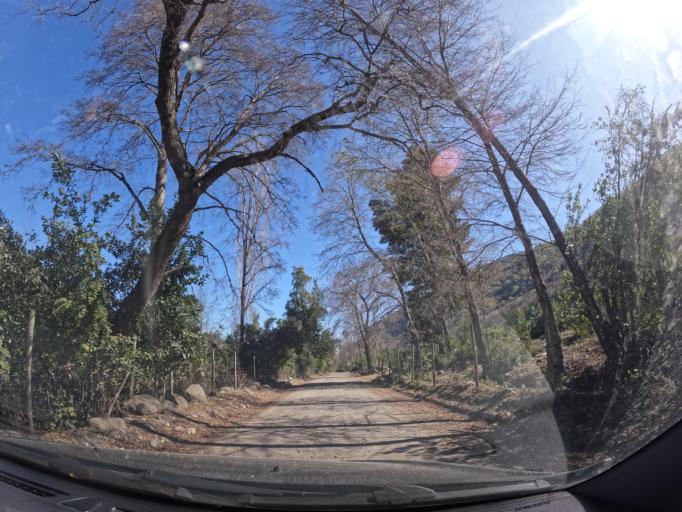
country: CL
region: Maule
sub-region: Provincia de Linares
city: Longavi
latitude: -36.2273
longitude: -71.3844
